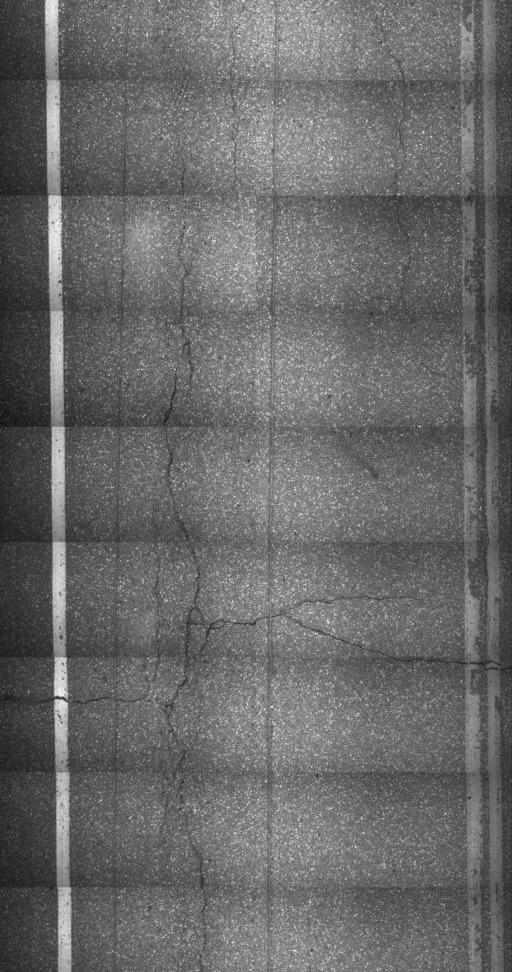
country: US
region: Vermont
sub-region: Caledonia County
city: Hardwick
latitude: 44.7403
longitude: -72.3769
